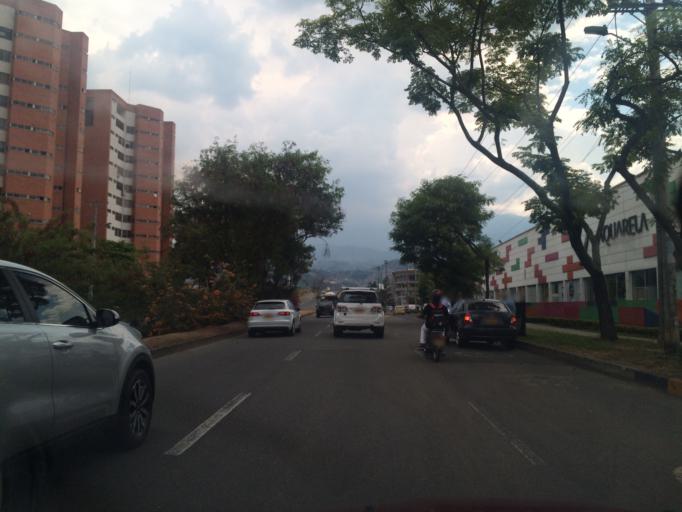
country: CO
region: Valle del Cauca
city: Cali
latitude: 3.3873
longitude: -76.5361
